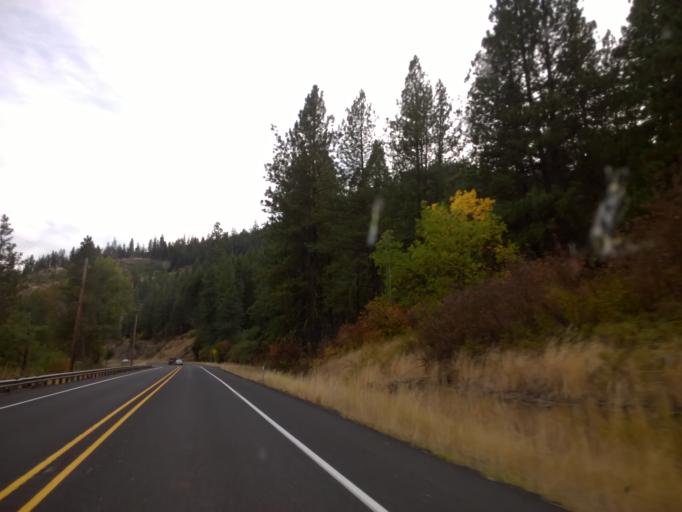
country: US
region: Washington
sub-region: Kittitas County
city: Cle Elum
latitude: 47.2444
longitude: -120.6972
